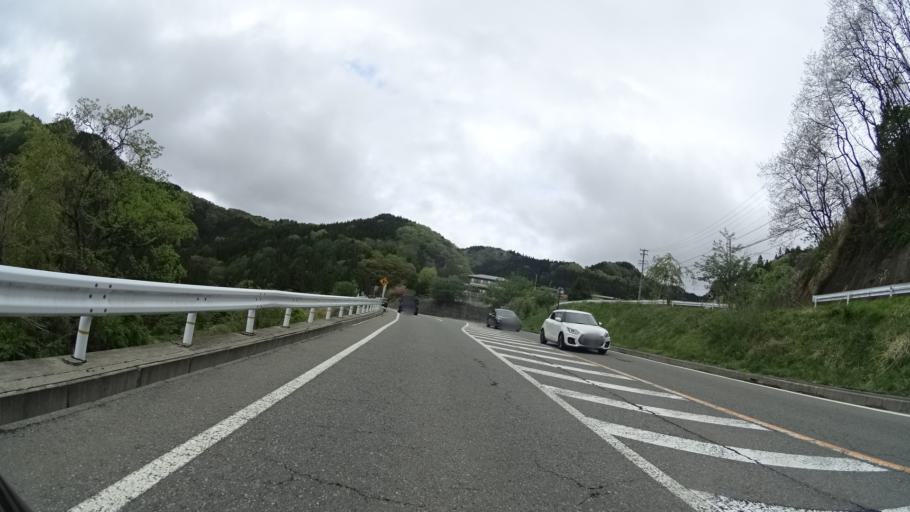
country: JP
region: Nagano
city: Nagano-shi
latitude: 36.7022
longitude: 138.2017
